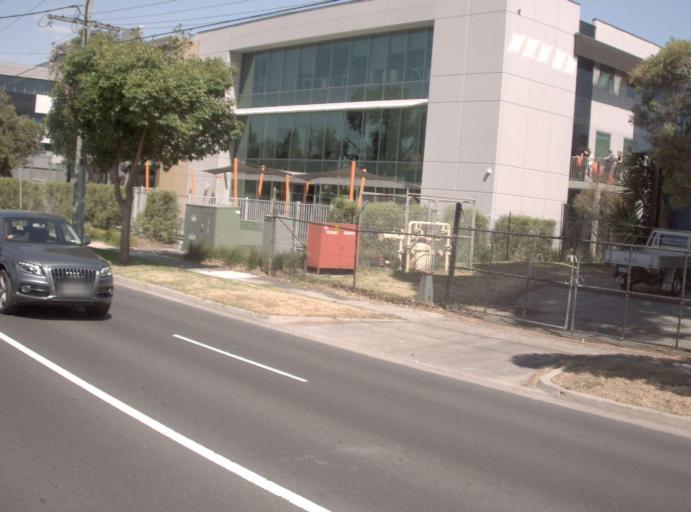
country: AU
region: Victoria
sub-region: Bayside
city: Highett
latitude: -37.9555
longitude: 145.0358
